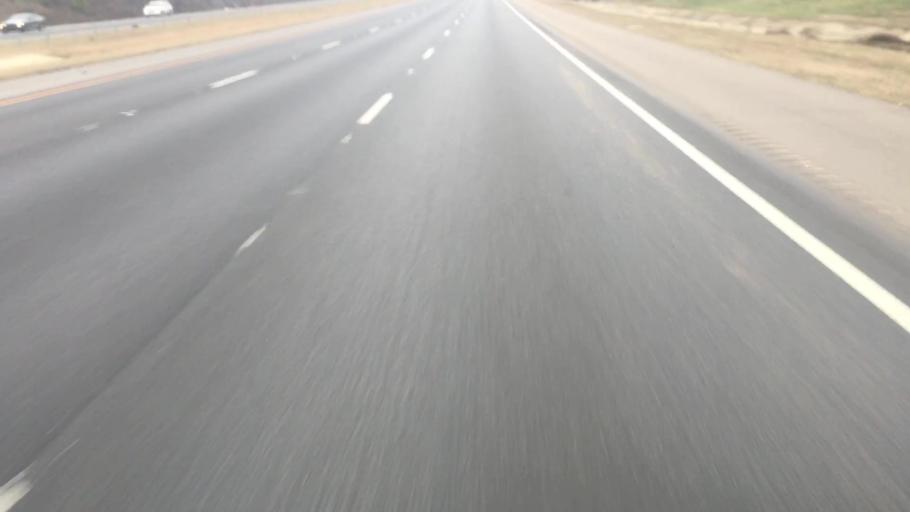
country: US
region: Alabama
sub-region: Jefferson County
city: Forestdale
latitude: 33.5879
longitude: -86.8459
